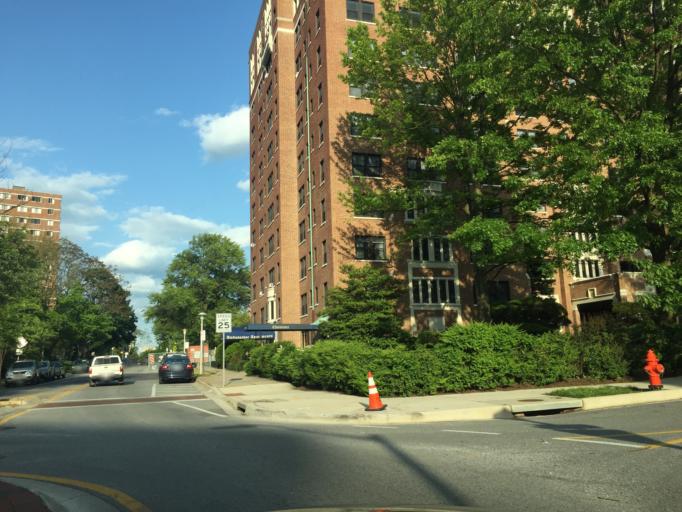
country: US
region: Maryland
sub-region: City of Baltimore
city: Baltimore
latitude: 39.3356
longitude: -76.6206
